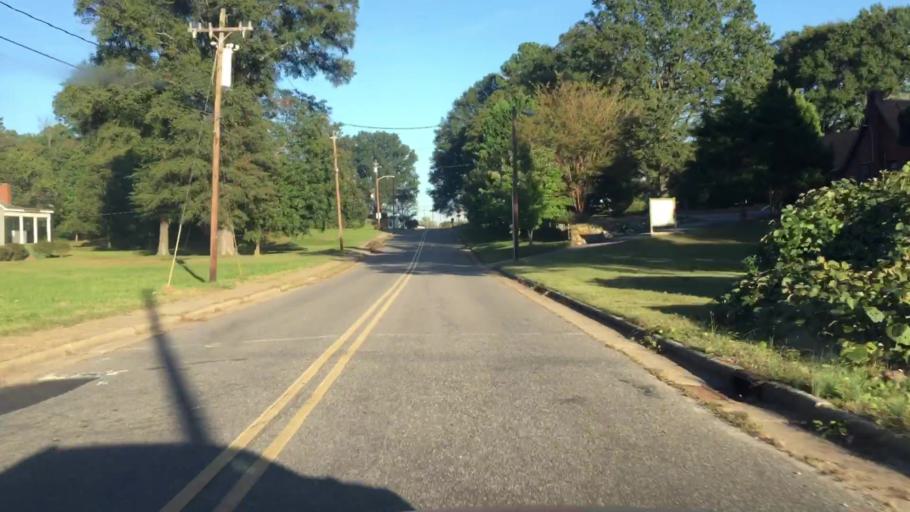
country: US
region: North Carolina
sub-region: Iredell County
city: Mooresville
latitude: 35.5759
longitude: -80.8063
